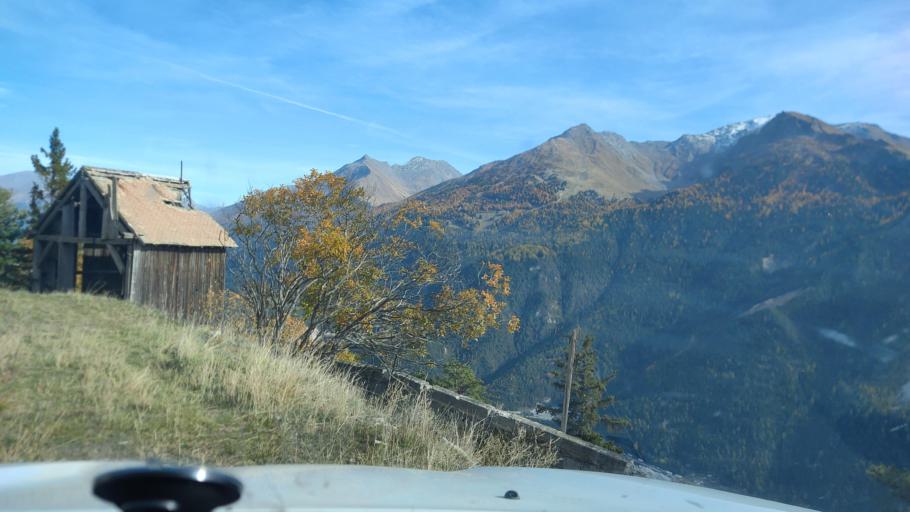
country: FR
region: Rhone-Alpes
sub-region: Departement de la Savoie
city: Modane
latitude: 45.2018
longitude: 6.6496
